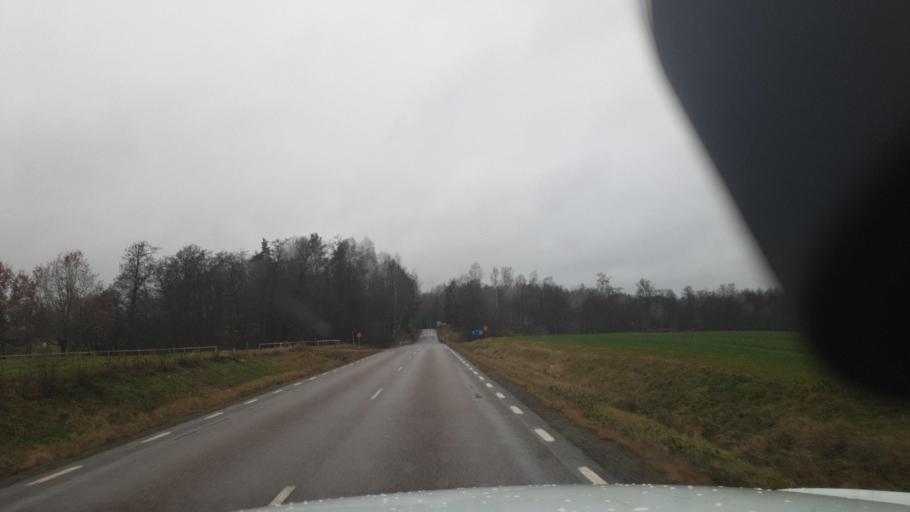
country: SE
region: Vaermland
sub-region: Arvika Kommun
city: Arvika
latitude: 59.5267
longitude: 12.6184
